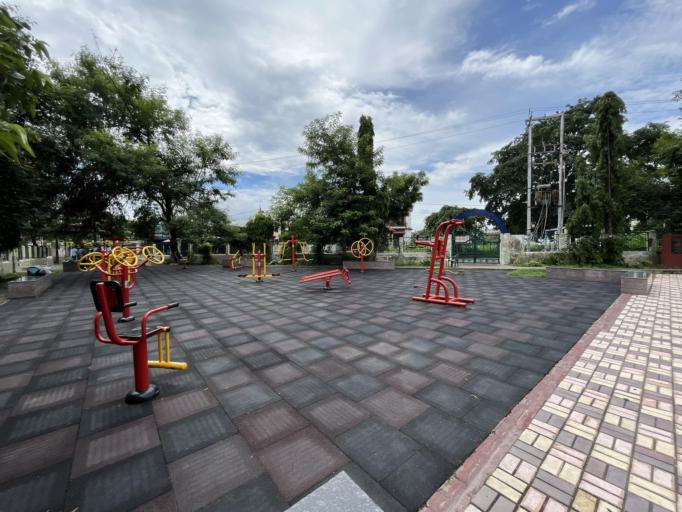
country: IN
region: Uttarakhand
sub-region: Naini Tal
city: Haldwani
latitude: 29.2108
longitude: 79.5176
